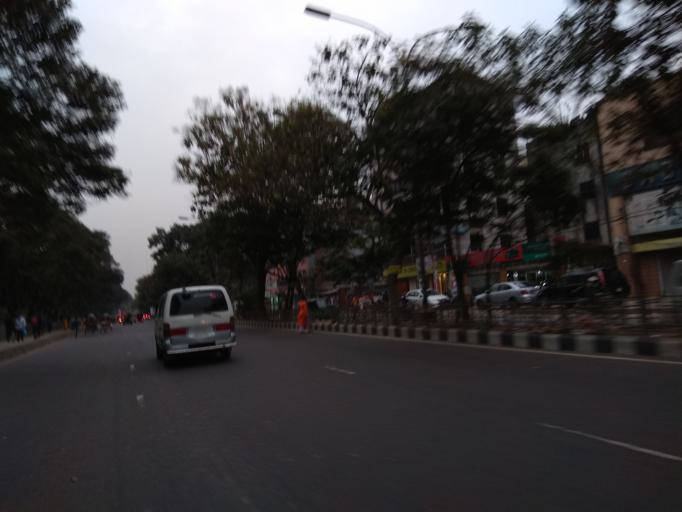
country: BD
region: Dhaka
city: Azimpur
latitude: 23.7626
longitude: 90.3834
